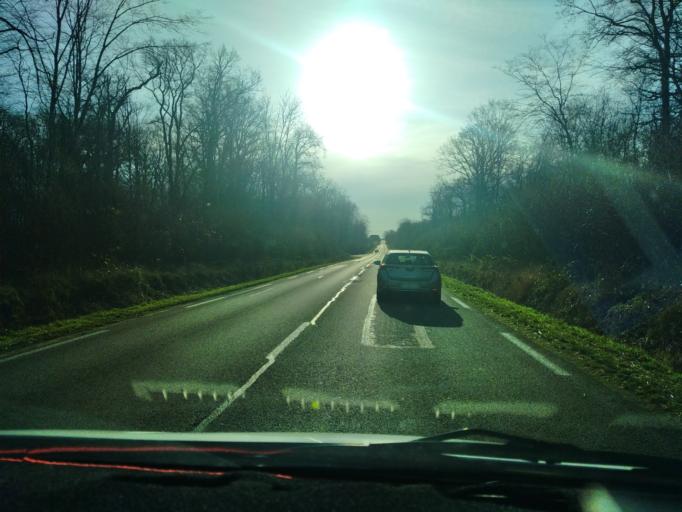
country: FR
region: Franche-Comte
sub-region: Departement de la Haute-Saone
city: Gray
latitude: 47.3810
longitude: 5.6599
